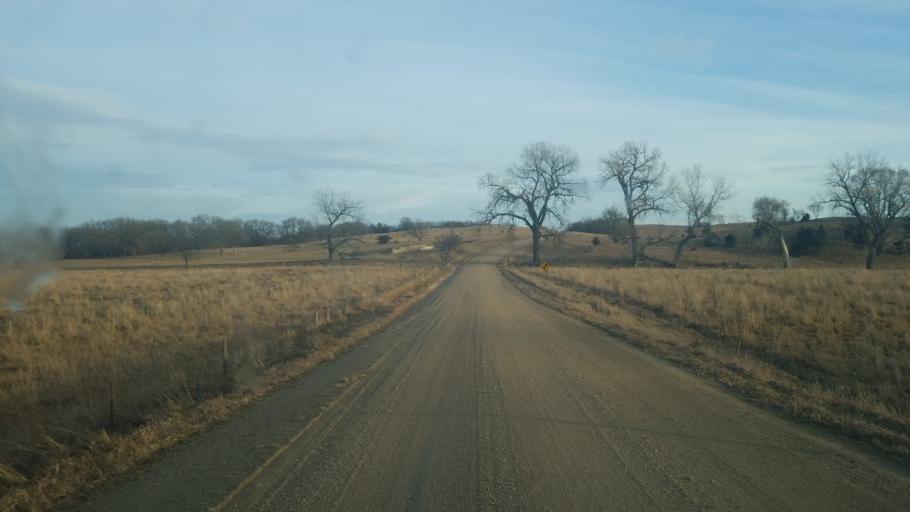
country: US
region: Nebraska
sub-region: Knox County
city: Center
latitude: 42.6955
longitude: -97.7874
